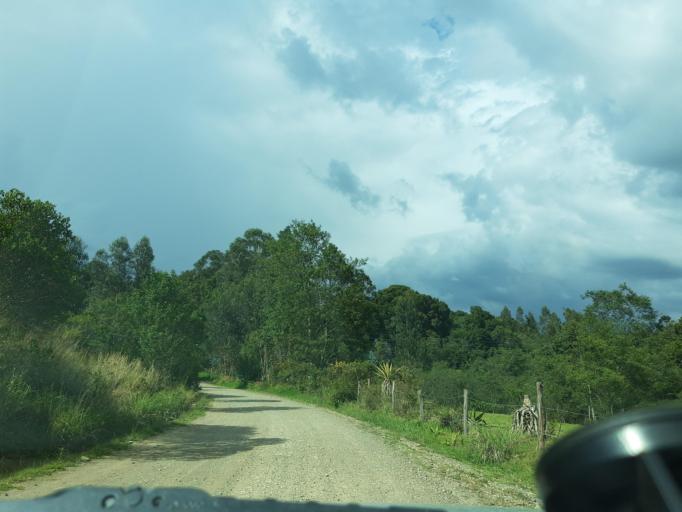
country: CO
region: Boyaca
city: Raquira
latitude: 5.5192
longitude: -73.6674
